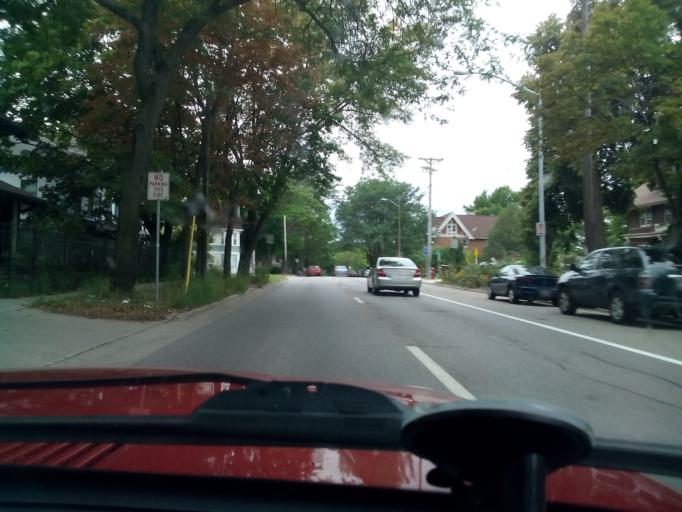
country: US
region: Wisconsin
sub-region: Dane County
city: Madison
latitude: 43.0830
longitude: -89.3800
